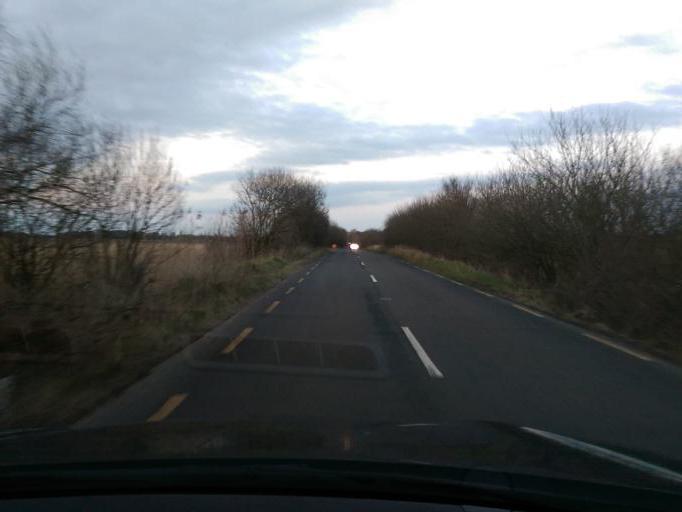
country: IE
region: Connaught
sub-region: County Galway
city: Portumna
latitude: 53.0614
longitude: -8.0930
